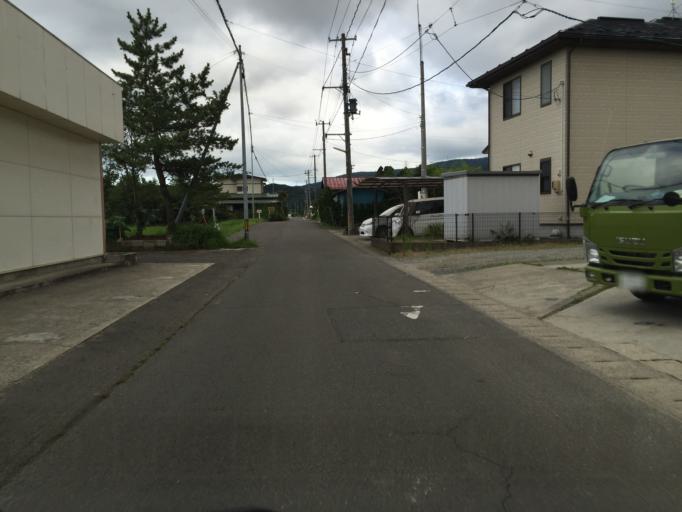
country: JP
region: Fukushima
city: Fukushima-shi
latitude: 37.7217
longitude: 140.3852
